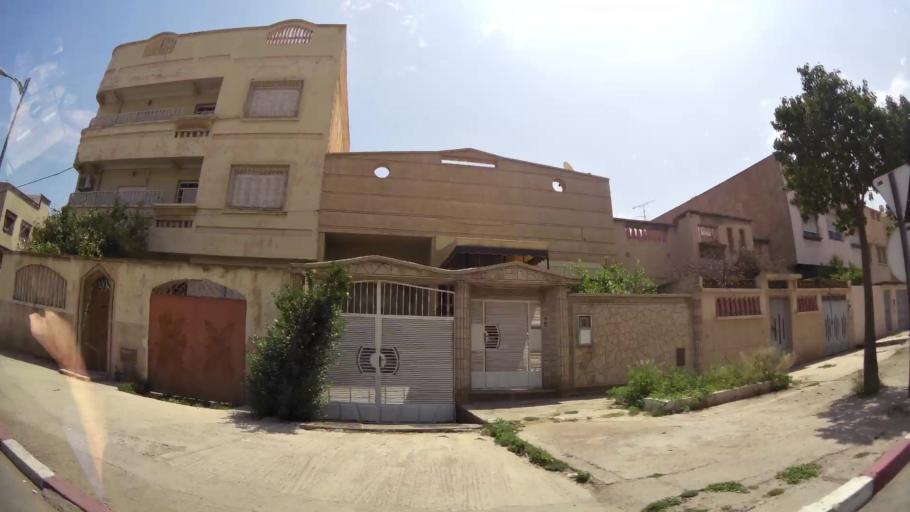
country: MA
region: Oriental
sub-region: Oujda-Angad
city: Oujda
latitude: 34.6897
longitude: -1.8916
